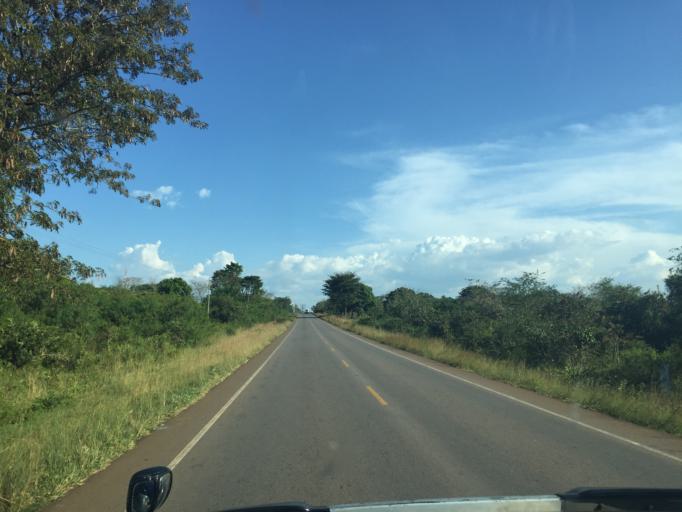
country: UG
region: Central Region
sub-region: Nakasongola District
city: Nakasongola
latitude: 1.2554
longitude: 32.4553
